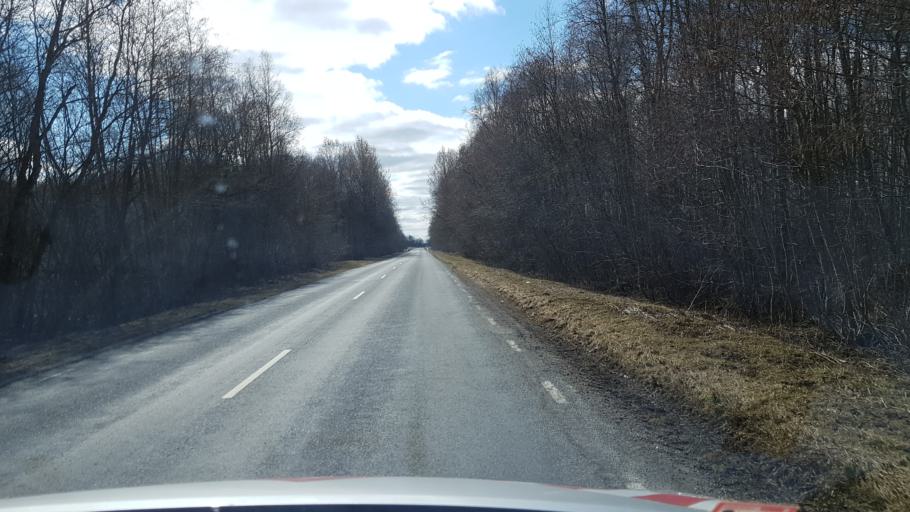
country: EE
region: Laeaene-Virumaa
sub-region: Tapa vald
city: Tapa
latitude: 59.2633
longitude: 25.8475
